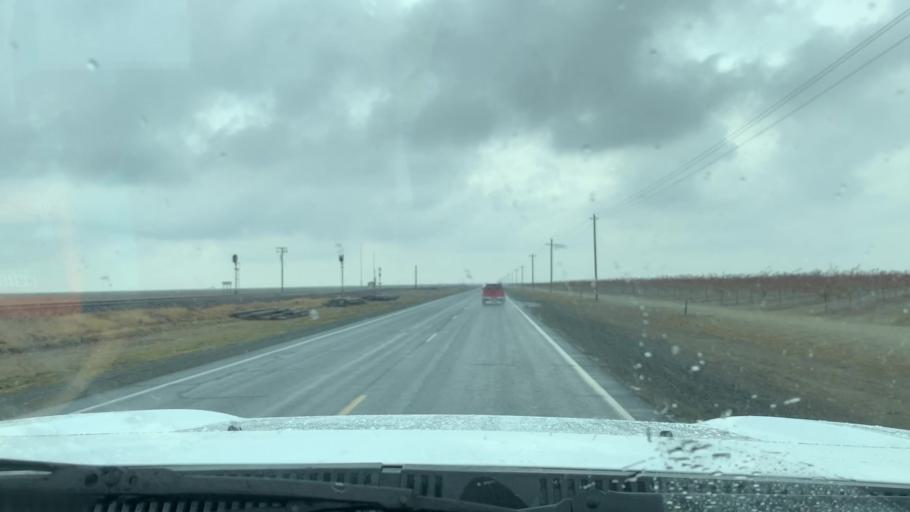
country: US
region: California
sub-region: Tulare County
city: Alpaugh
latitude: 35.9971
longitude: -119.4825
